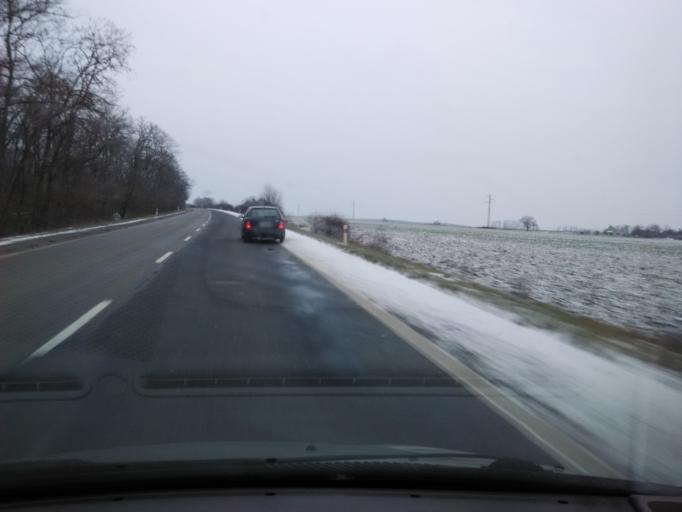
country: SK
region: Nitriansky
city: Zlate Moravce
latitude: 48.3652
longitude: 18.4477
